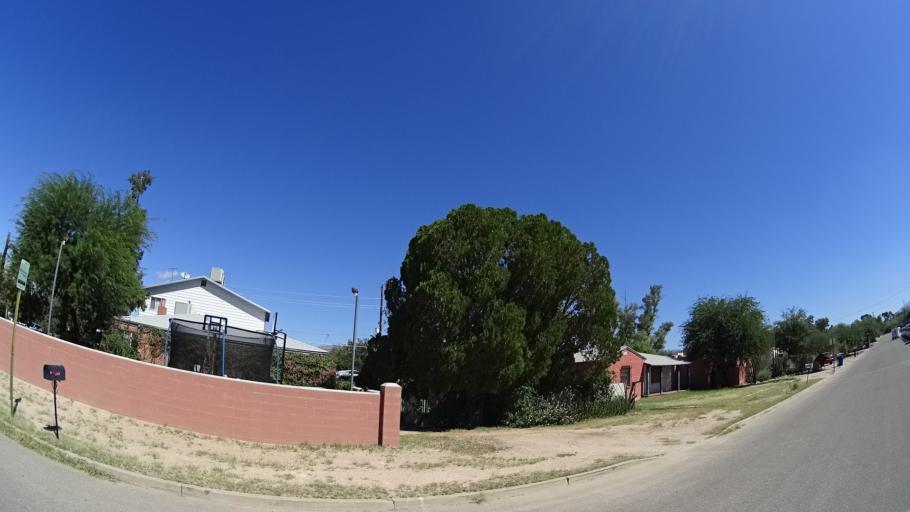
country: US
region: Arizona
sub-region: Pima County
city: Tucson
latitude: 32.2437
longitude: -110.9466
